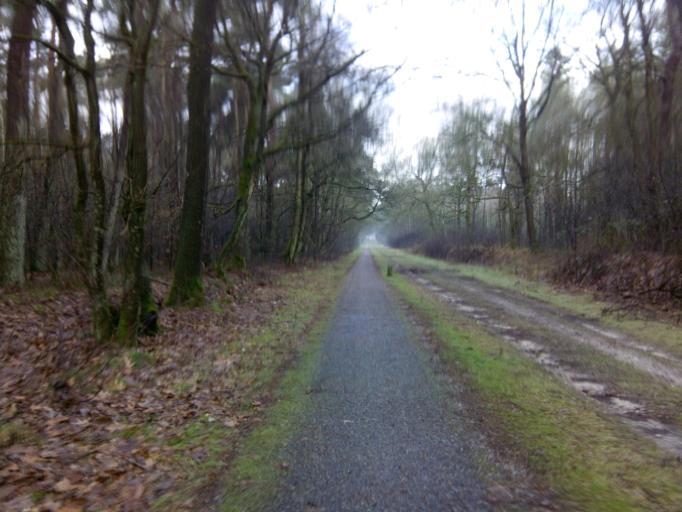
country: NL
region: Utrecht
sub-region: Gemeente Utrechtse Heuvelrug
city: Overberg
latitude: 52.0081
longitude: 5.5018
